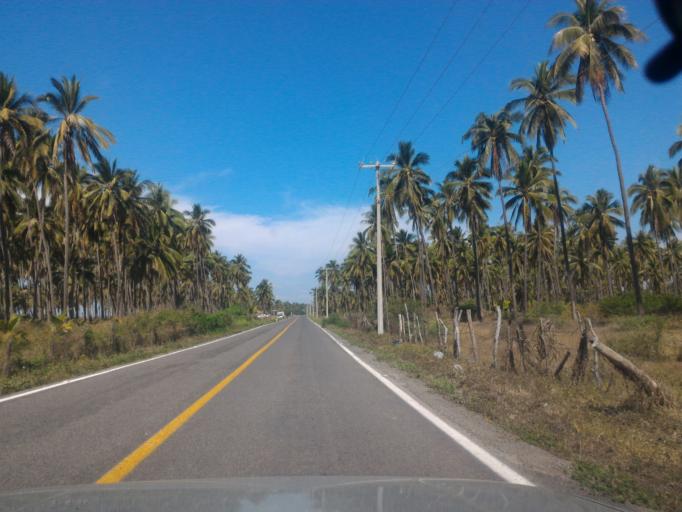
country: MX
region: Colima
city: Armeria
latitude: 18.8513
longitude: -103.9561
